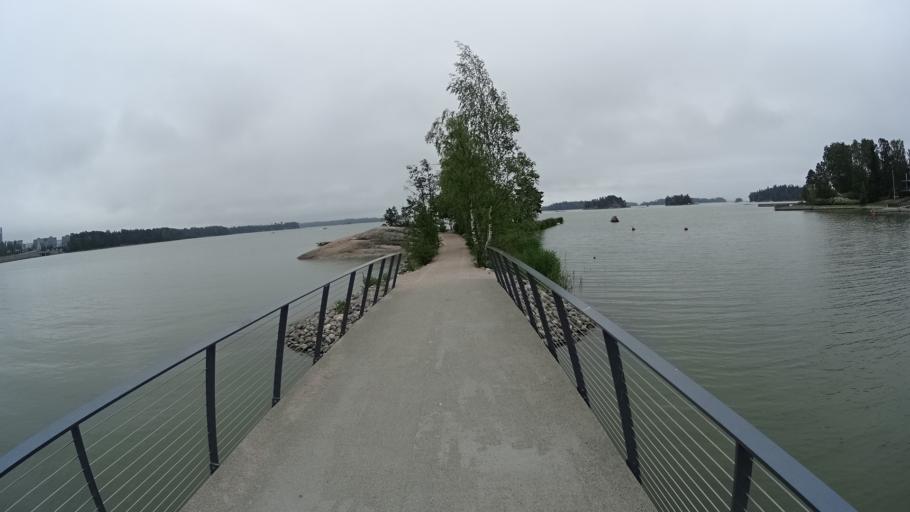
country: FI
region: Uusimaa
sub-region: Helsinki
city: Otaniemi
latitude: 60.1677
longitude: 24.8103
